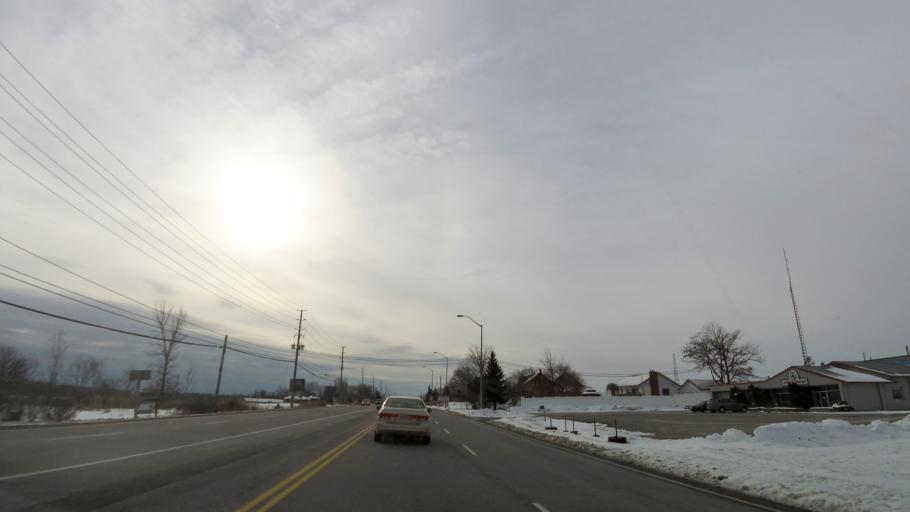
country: CA
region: Ontario
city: Hamilton
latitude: 43.3103
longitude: -79.9201
